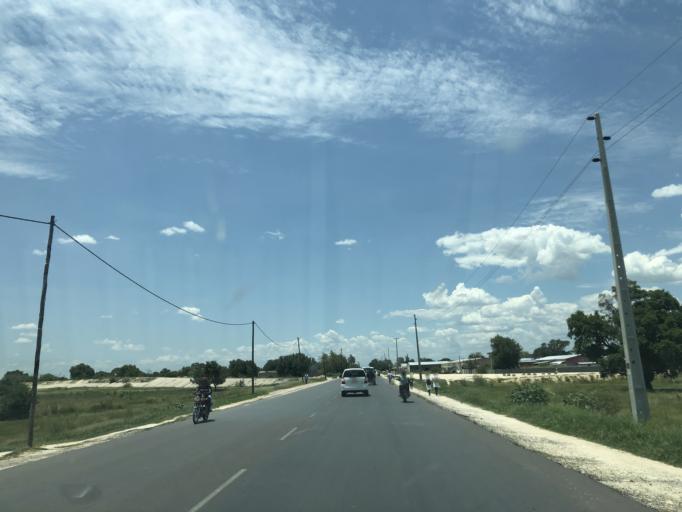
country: AO
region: Cunene
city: Ondjiva
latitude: -17.0592
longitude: 15.7398
